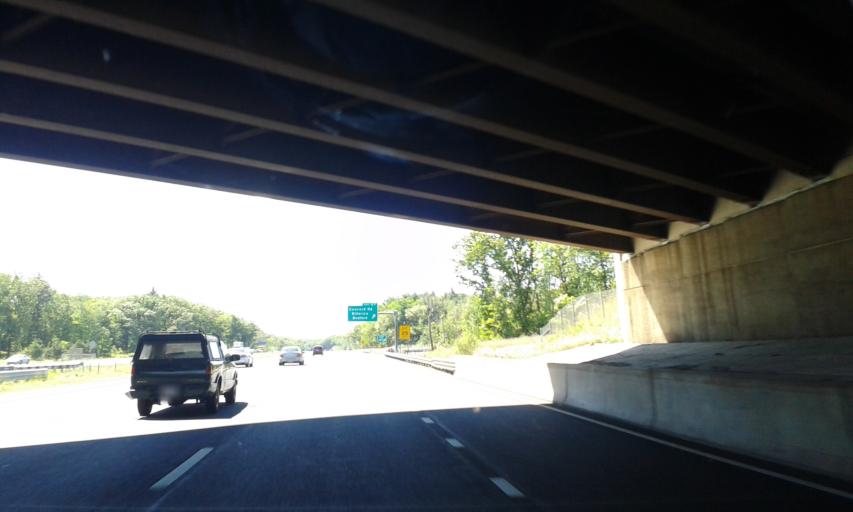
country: US
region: Massachusetts
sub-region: Middlesex County
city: Billerica
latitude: 42.5431
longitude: -71.2841
